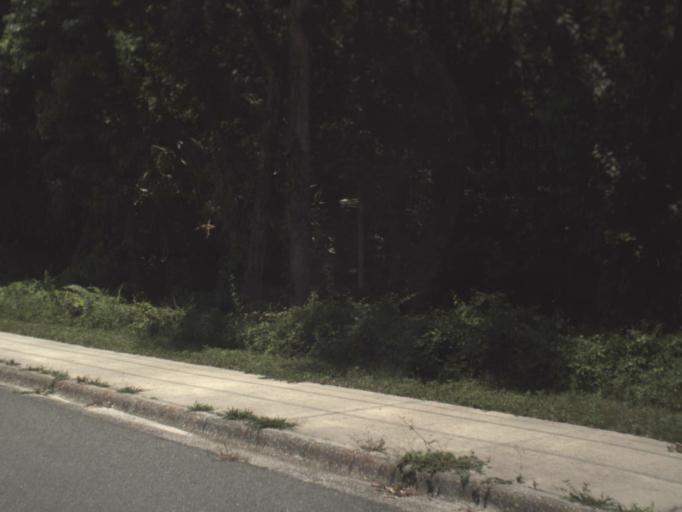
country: US
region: Florida
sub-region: Citrus County
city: Crystal River
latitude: 28.9019
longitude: -82.6010
